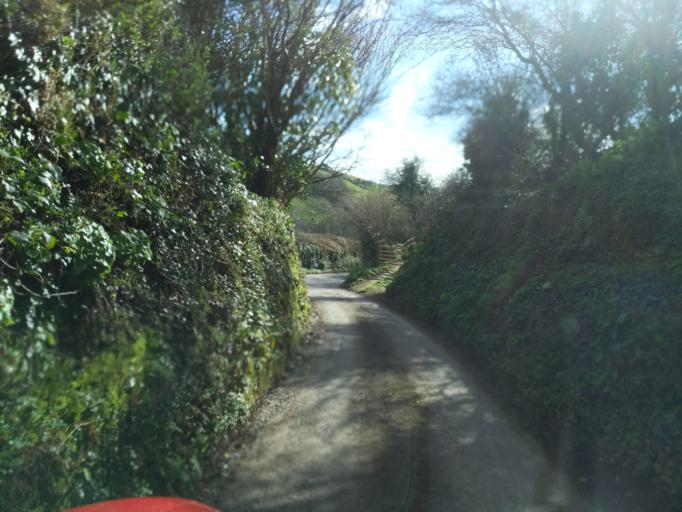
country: GB
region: England
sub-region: Devon
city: Kingsbridge
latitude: 50.2877
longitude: -3.7544
